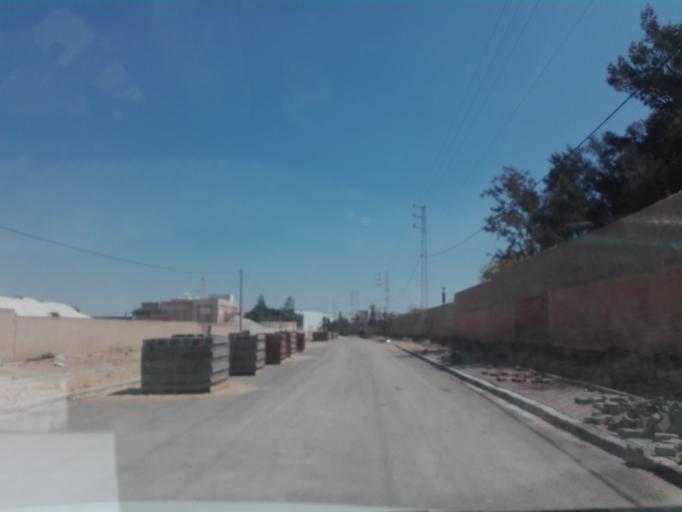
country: TN
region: Safaqis
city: Sfax
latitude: 34.7239
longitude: 10.5154
